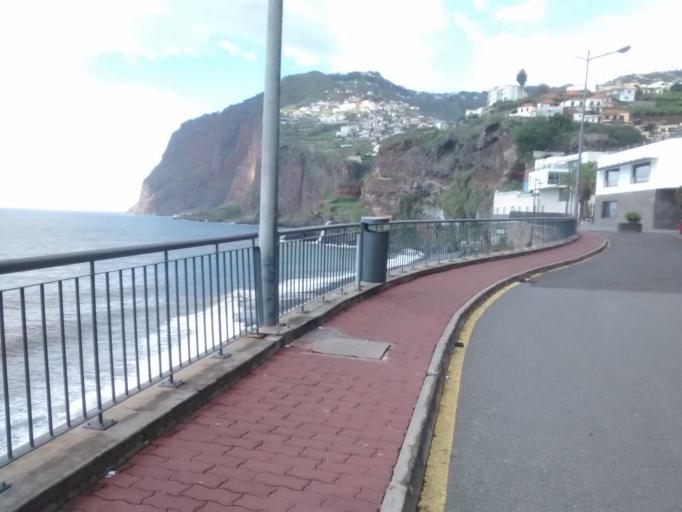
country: PT
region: Madeira
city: Camara de Lobos
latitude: 32.6480
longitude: -16.9778
